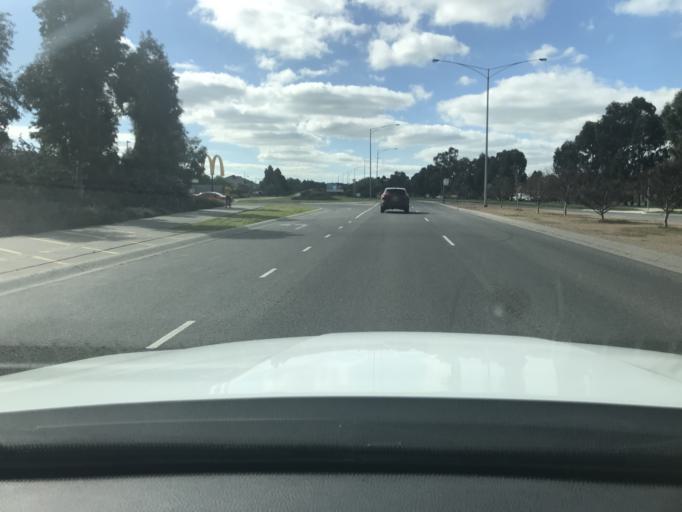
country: AU
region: Victoria
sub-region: Hume
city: Craigieburn
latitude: -37.5747
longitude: 144.9207
